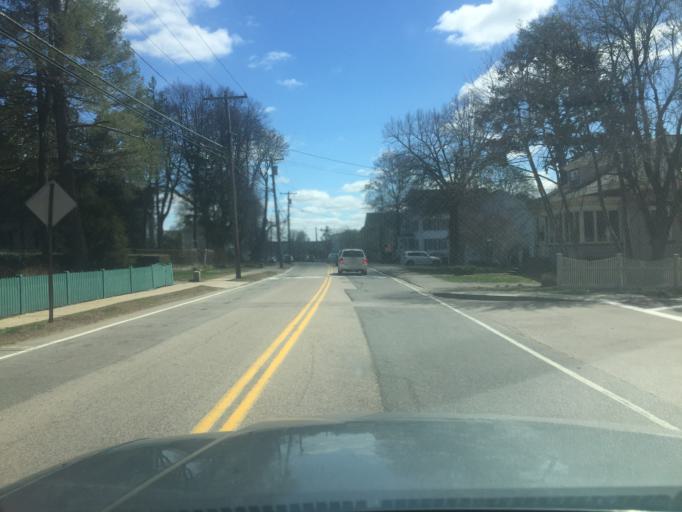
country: US
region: Massachusetts
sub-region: Norfolk County
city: Medfield
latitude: 42.1913
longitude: -71.3093
